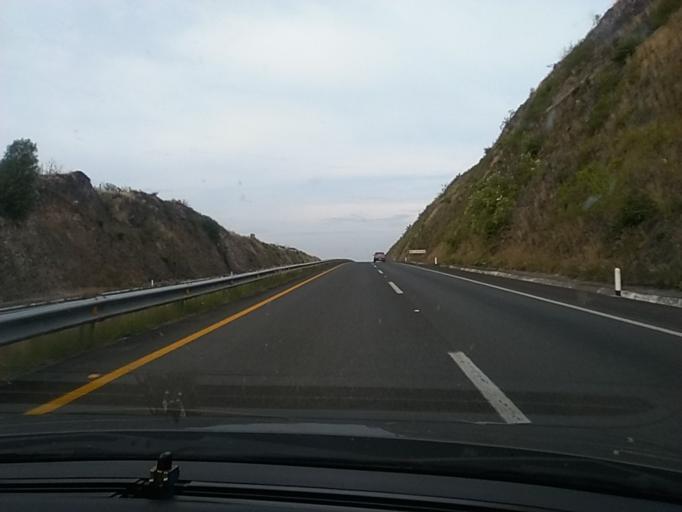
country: MX
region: Michoacan
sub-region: Zinapecuaro
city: Francisco Villa
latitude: 19.8831
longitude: -100.9250
